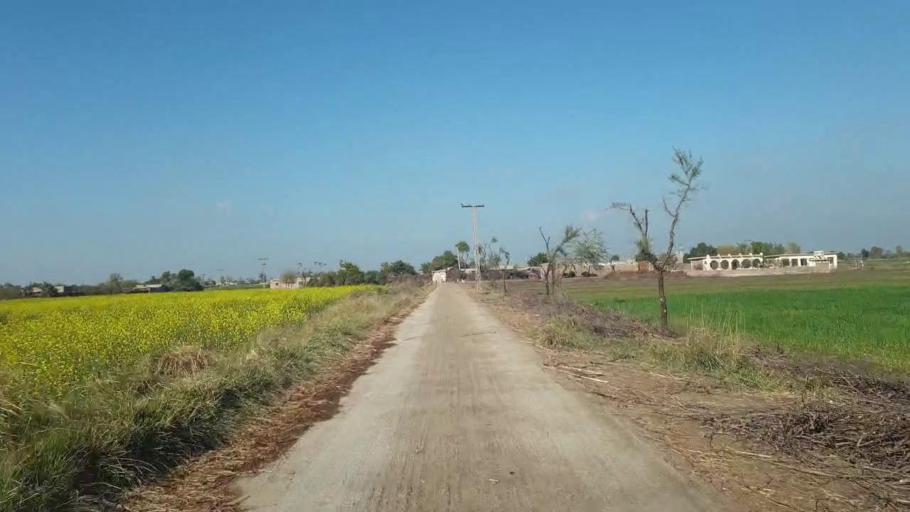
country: PK
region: Sindh
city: Shahdadpur
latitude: 25.9315
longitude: 68.5302
